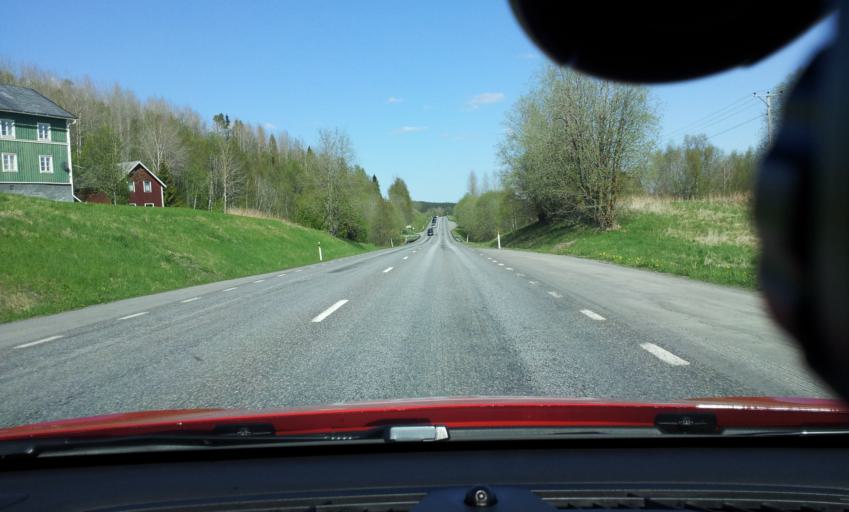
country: SE
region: Jaemtland
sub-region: Are Kommun
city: Jarpen
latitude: 63.3146
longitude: 13.3420
